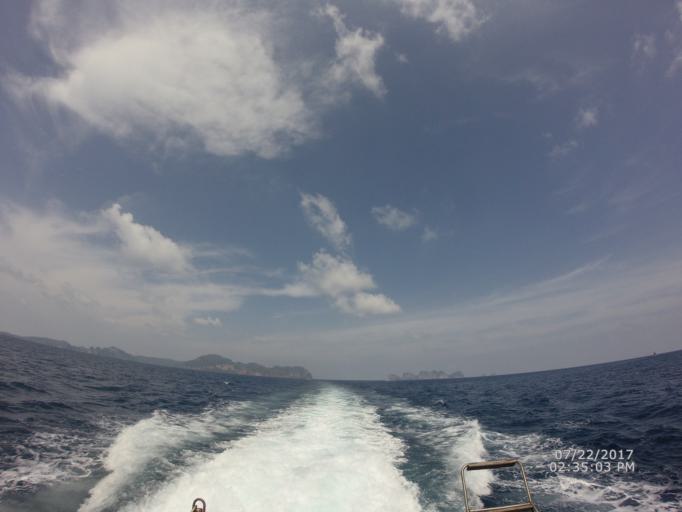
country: TH
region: Phangnga
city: Ban Phru Nai
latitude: 7.7436
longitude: 98.7047
